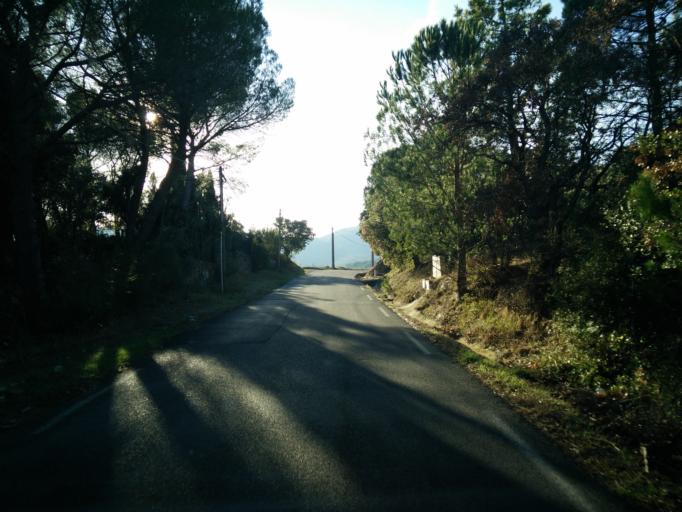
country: FR
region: Provence-Alpes-Cote d'Azur
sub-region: Departement du Var
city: Le Plan-de-la-Tour
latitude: 43.3373
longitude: 6.5406
